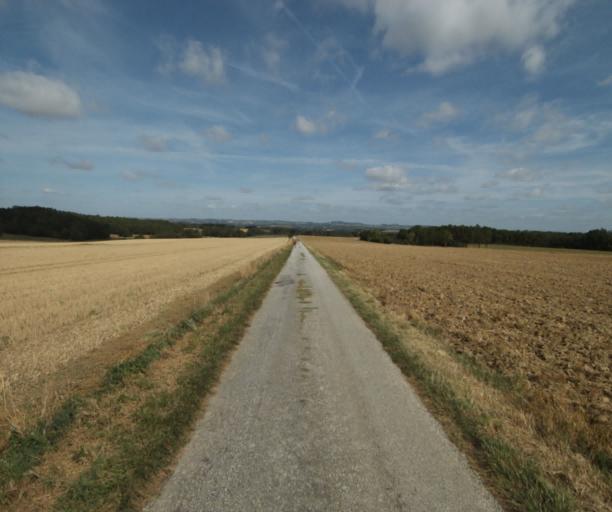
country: FR
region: Midi-Pyrenees
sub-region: Departement du Tarn
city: Soreze
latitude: 43.4716
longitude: 2.1007
